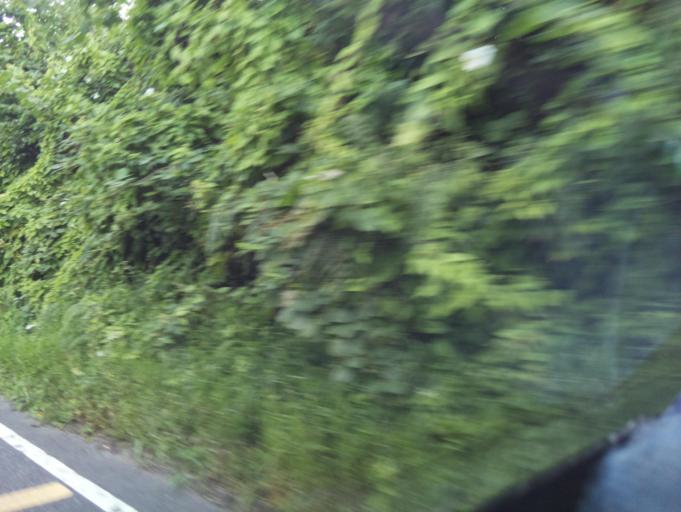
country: GB
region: England
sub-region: North Somerset
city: Easton-in-Gordano
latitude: 51.4708
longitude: -2.7197
